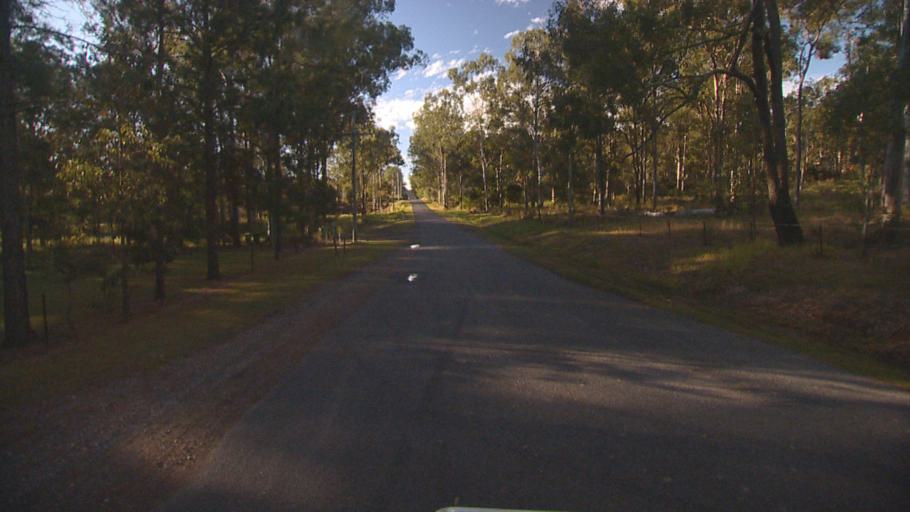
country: AU
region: Queensland
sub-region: Logan
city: Windaroo
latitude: -27.7368
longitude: 153.1509
